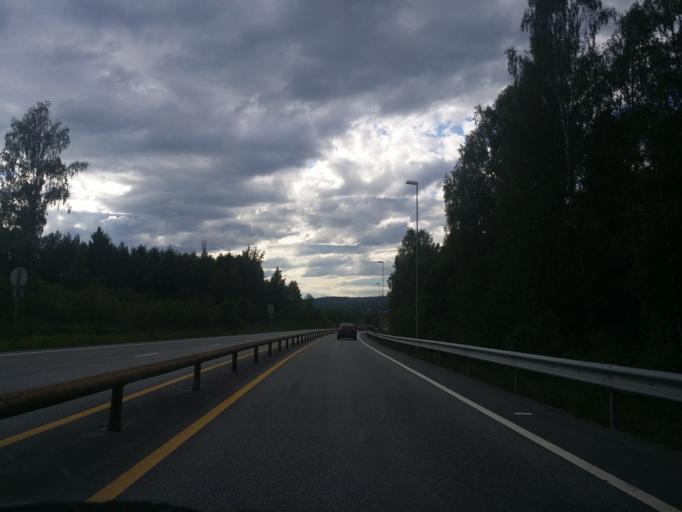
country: NO
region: Hedmark
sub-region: Hamar
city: Hamar
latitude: 60.7823
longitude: 11.1360
